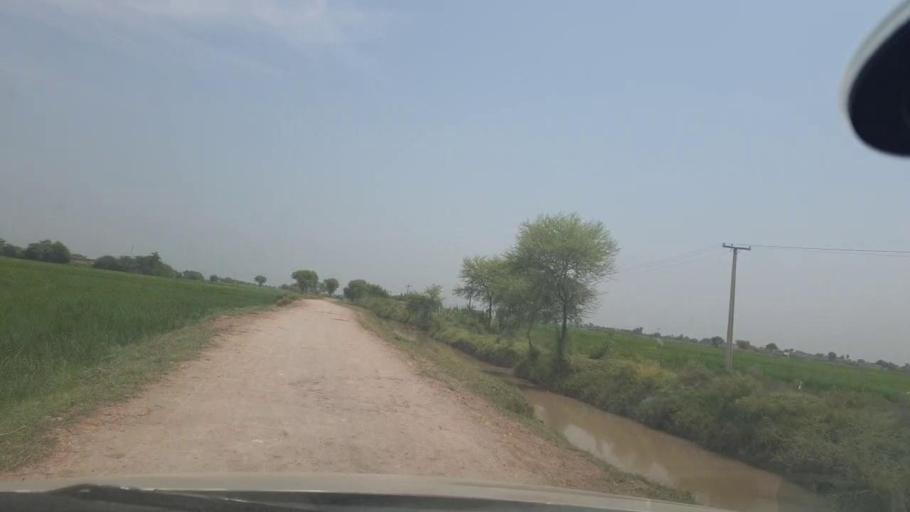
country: PK
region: Sindh
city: Jacobabad
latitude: 28.1675
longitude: 68.3945
